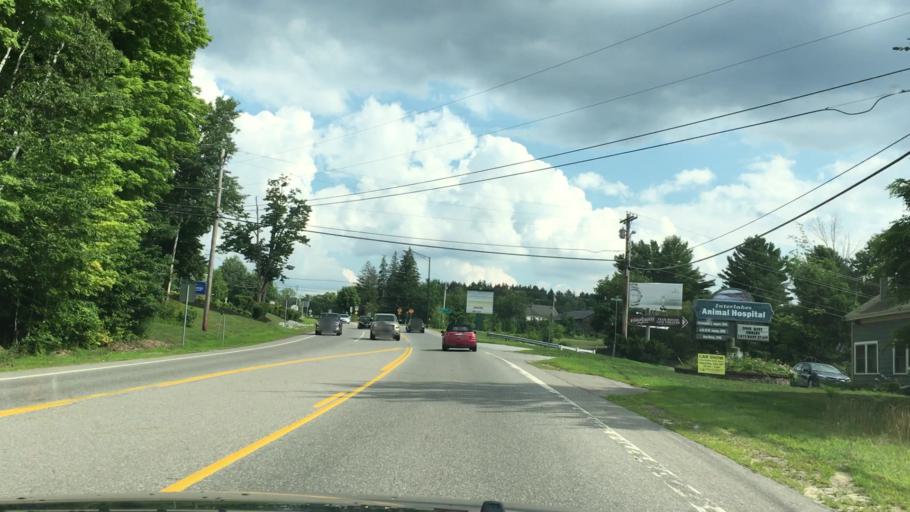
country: US
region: New Hampshire
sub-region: Belknap County
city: Meredith
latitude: 43.6420
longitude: -71.5007
